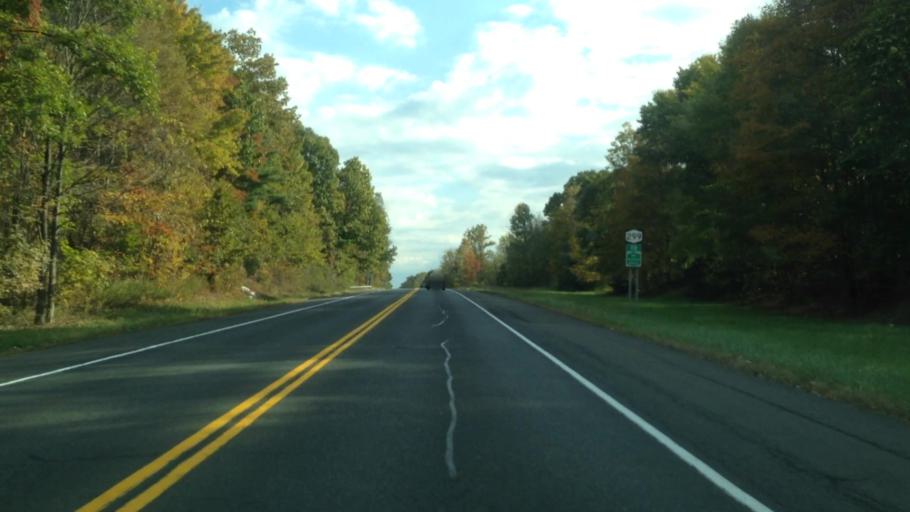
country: US
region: New York
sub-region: Ulster County
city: Highland
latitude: 41.7390
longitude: -74.0103
